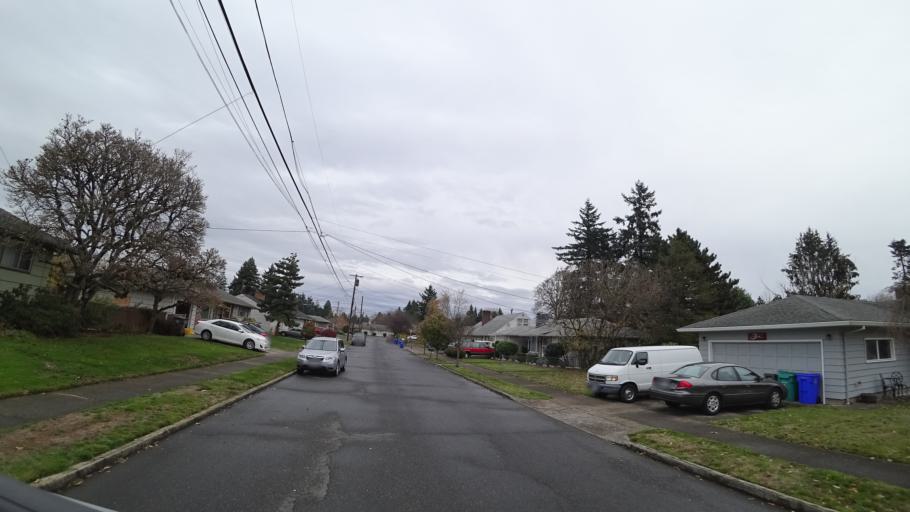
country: US
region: Oregon
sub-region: Multnomah County
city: Lents
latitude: 45.5145
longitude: -122.5393
